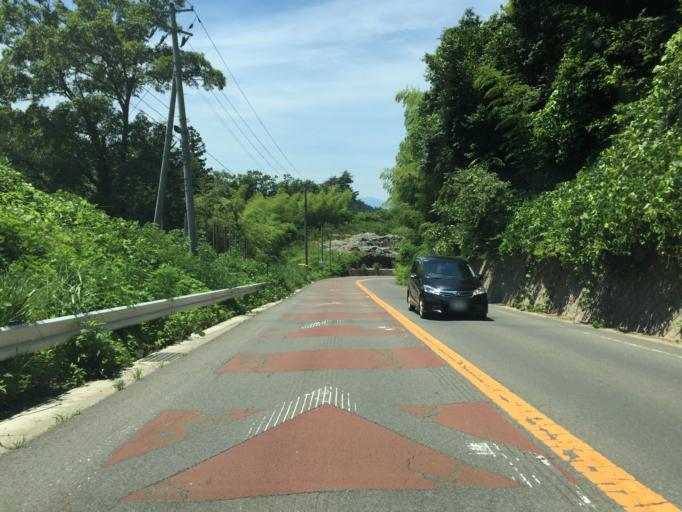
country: JP
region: Fukushima
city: Fukushima-shi
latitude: 37.7504
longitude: 140.5243
